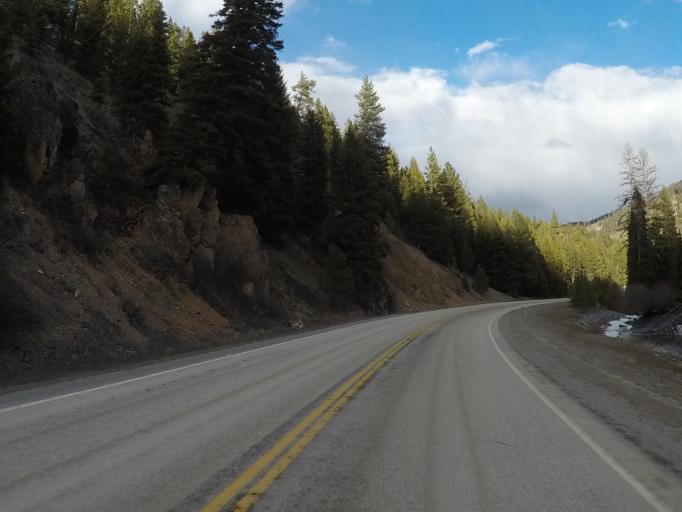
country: US
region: Montana
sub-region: Missoula County
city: Frenchtown
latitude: 46.7520
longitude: -114.5119
